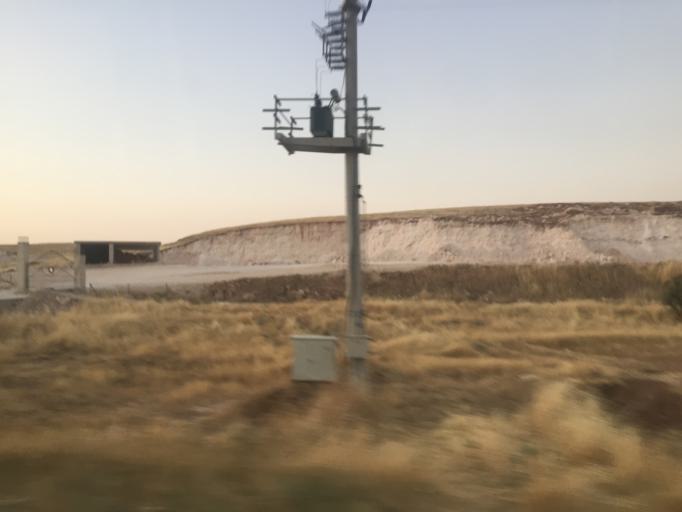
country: TR
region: Mardin
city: Kindirip
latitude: 37.4619
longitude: 41.2324
